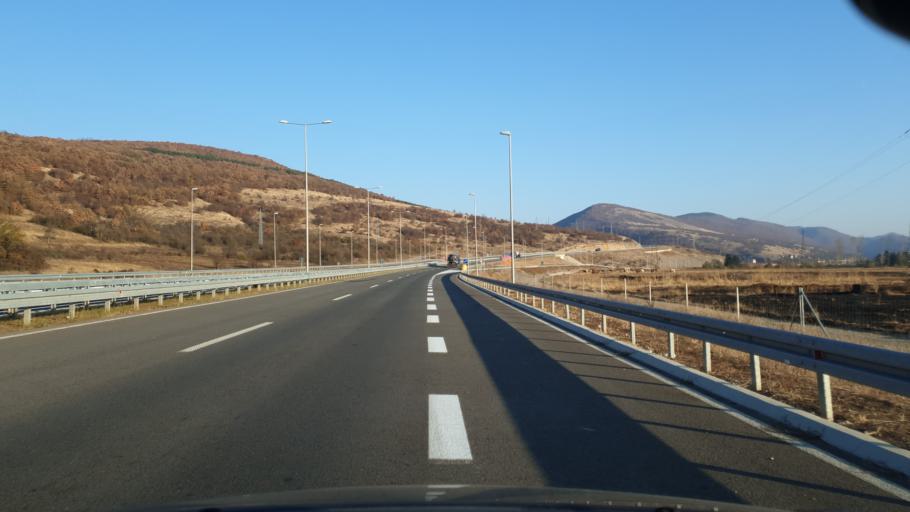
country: RS
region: Central Serbia
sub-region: Pirotski Okrug
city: Dimitrovgrad
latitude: 43.0208
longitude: 22.7412
